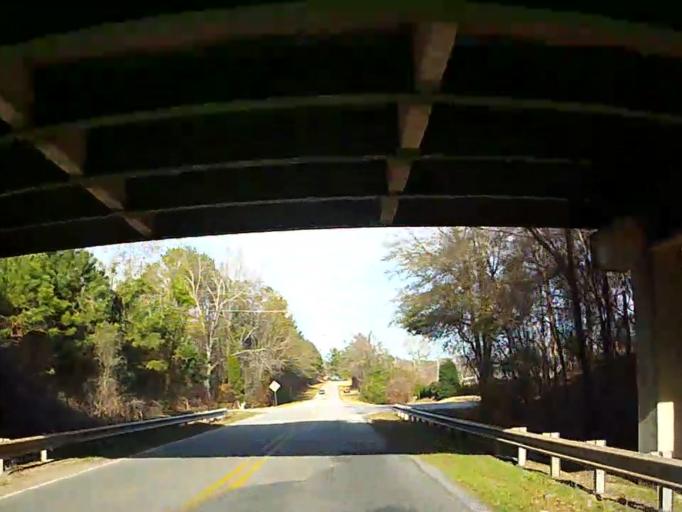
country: US
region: Georgia
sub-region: Bibb County
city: West Point
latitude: 32.9475
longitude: -83.7963
